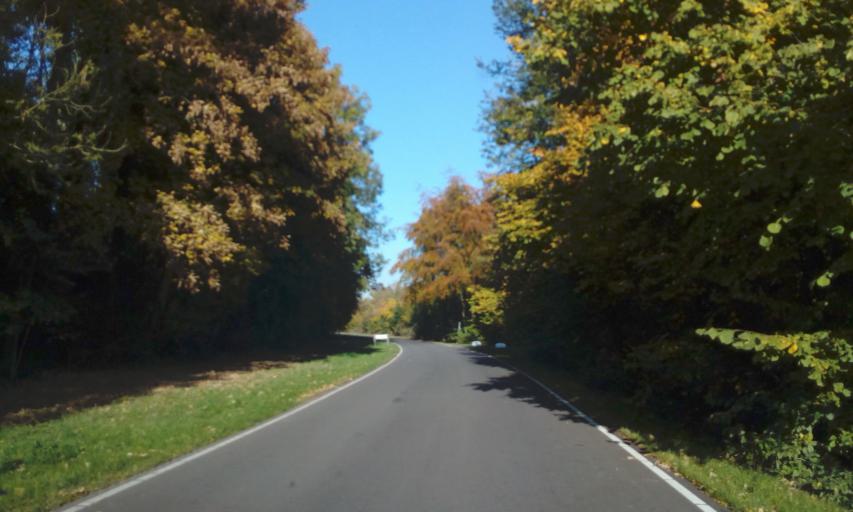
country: NL
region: South Holland
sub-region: Gemeente Lansingerland
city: Bleiswijk
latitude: 52.0124
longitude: 4.5503
